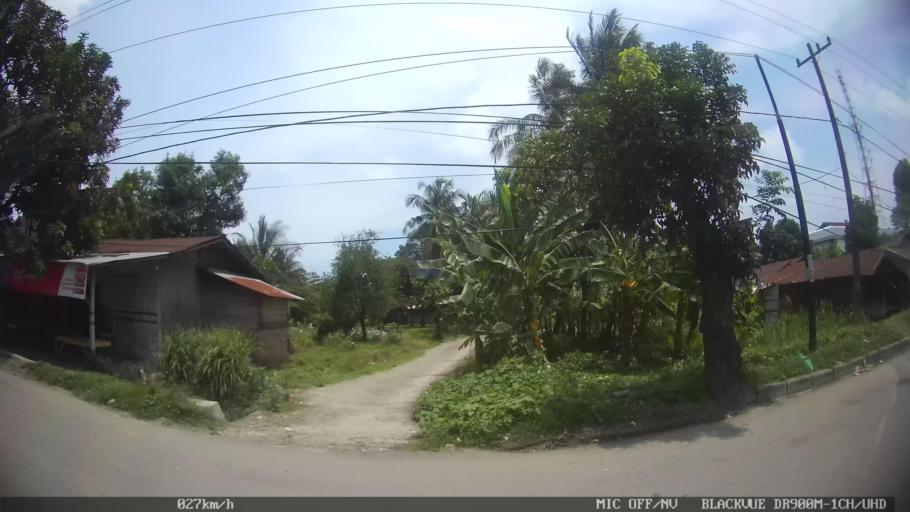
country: ID
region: North Sumatra
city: Labuhan Deli
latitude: 3.7112
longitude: 98.6797
